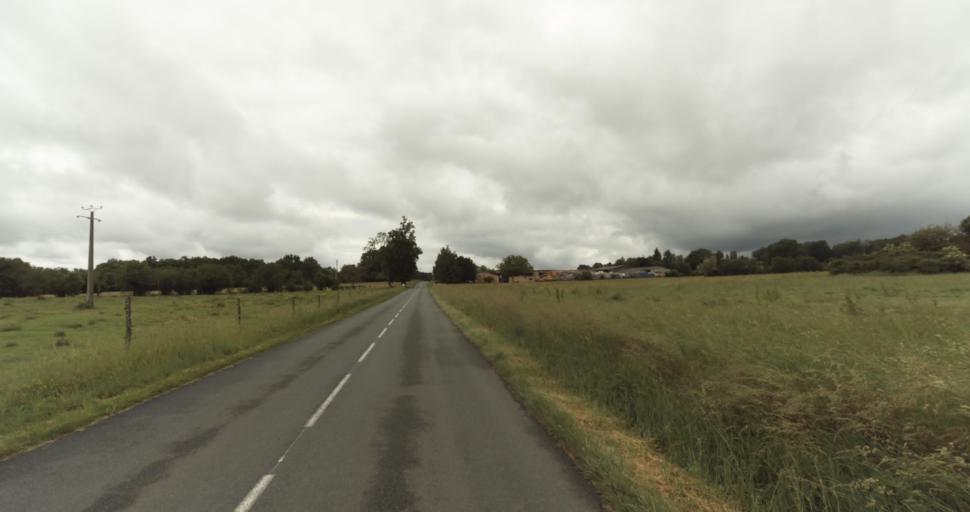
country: FR
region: Aquitaine
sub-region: Departement de la Dordogne
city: Belves
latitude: 44.6914
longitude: 0.9079
